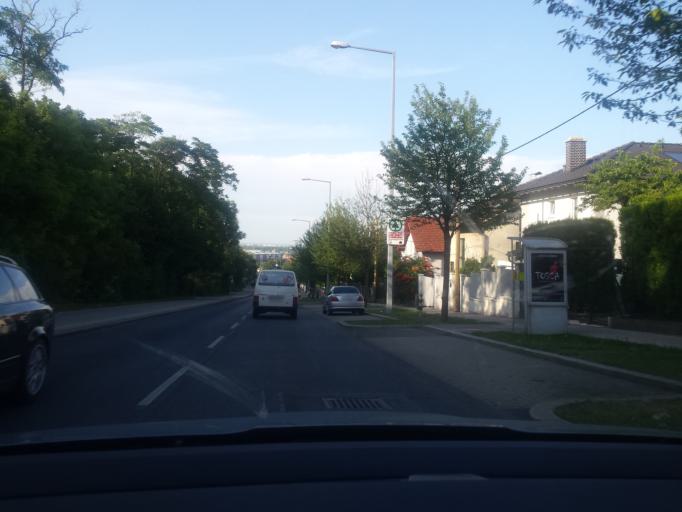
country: AT
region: Lower Austria
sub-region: Politischer Bezirk Wien-Umgebung
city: Leopoldsdorf
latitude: 48.1616
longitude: 16.4079
